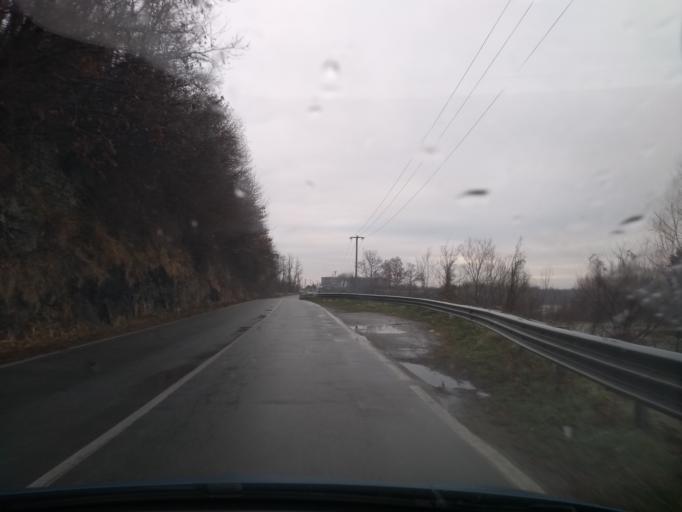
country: IT
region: Piedmont
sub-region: Provincia di Torino
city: Valperga
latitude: 45.3889
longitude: 7.6712
